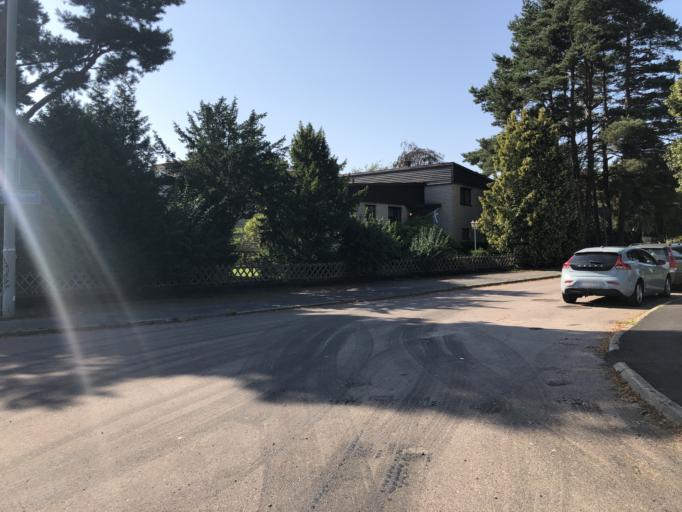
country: SE
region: Vaestra Goetaland
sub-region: Goteborg
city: Goeteborg
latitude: 57.7417
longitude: 11.9682
